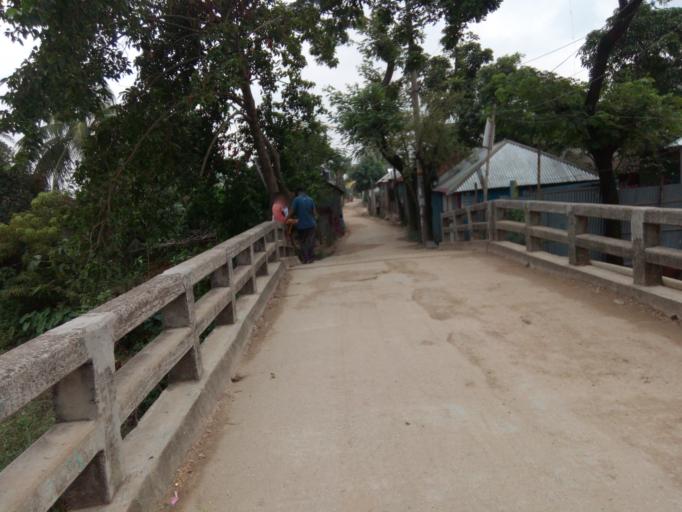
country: BD
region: Dhaka
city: Paltan
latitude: 23.7436
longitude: 90.4615
